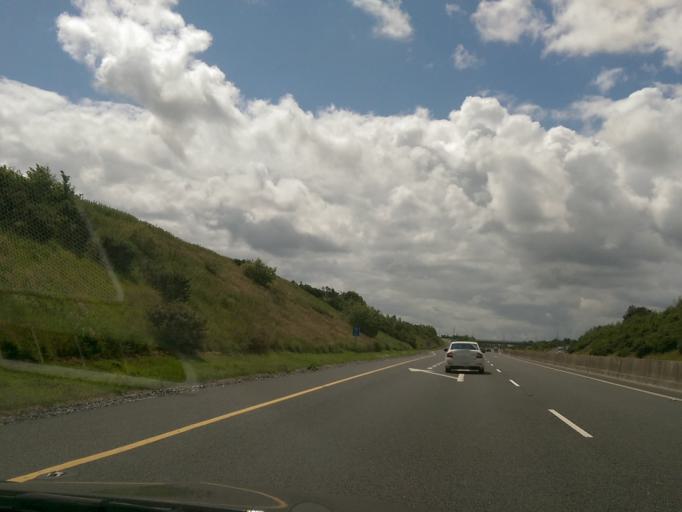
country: IE
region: Munster
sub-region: County Cork
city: Mitchelstown
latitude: 52.2872
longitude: -8.2102
